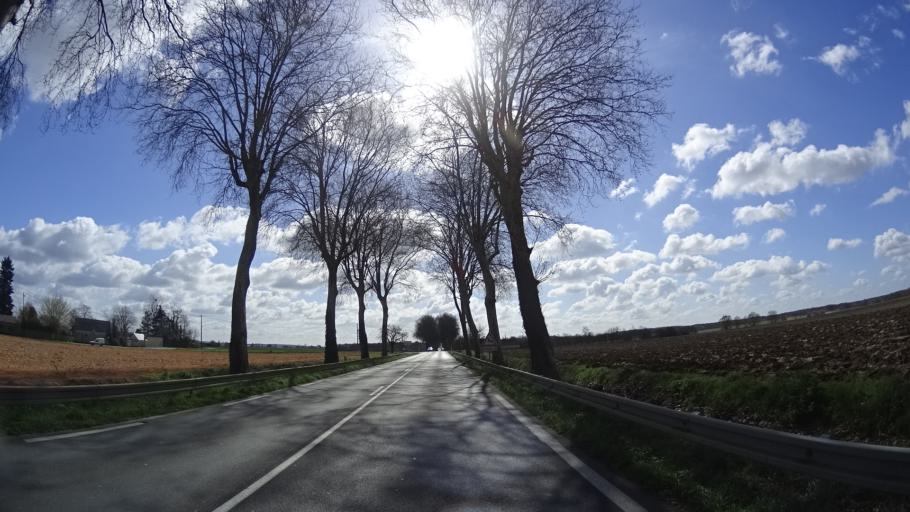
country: FR
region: Pays de la Loire
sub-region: Departement de Maine-et-Loire
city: Brissac-Quince
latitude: 47.3157
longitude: -0.4051
